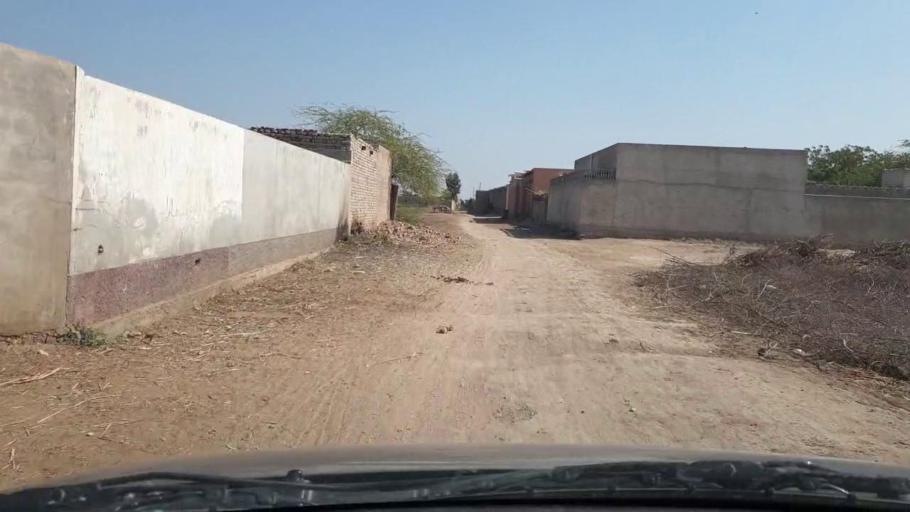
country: PK
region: Sindh
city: Samaro
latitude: 25.2444
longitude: 69.2456
